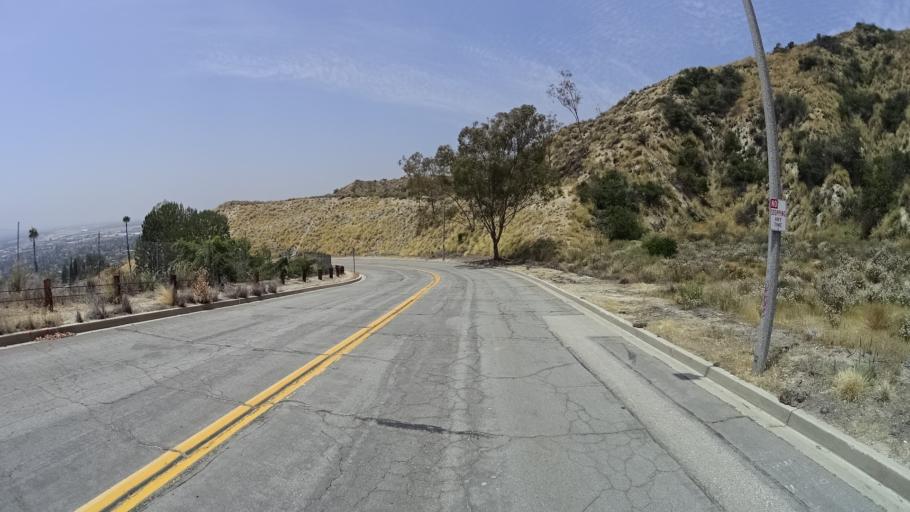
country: US
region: California
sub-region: Los Angeles County
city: Burbank
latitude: 34.2048
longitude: -118.3166
